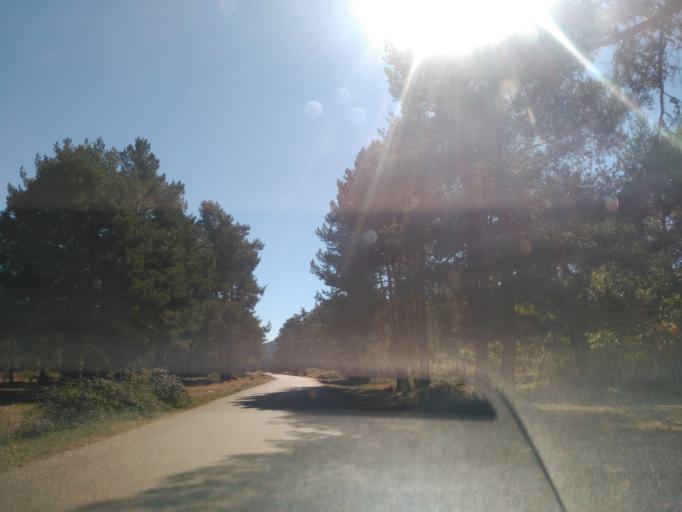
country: ES
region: Castille and Leon
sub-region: Provincia de Soria
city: Vinuesa
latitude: 41.9524
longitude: -2.7815
